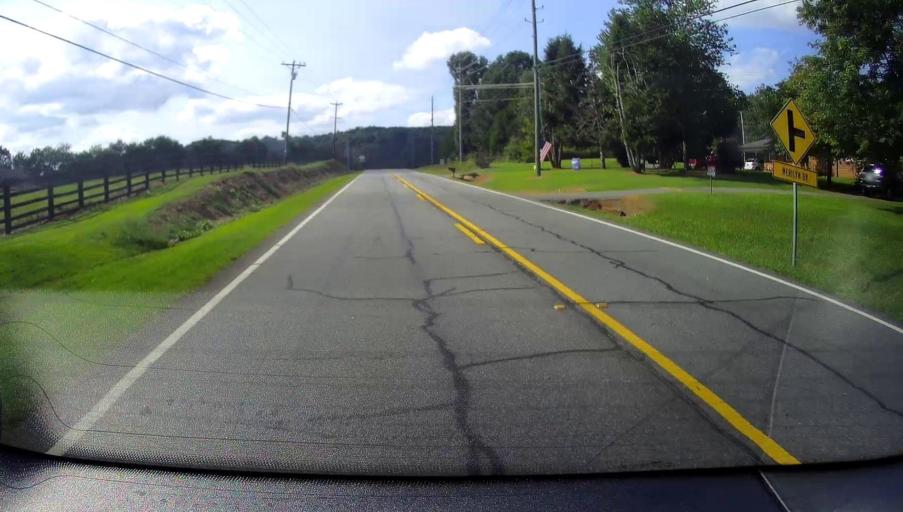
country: US
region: Georgia
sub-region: Catoosa County
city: Ringgold
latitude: 34.9094
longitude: -85.0828
